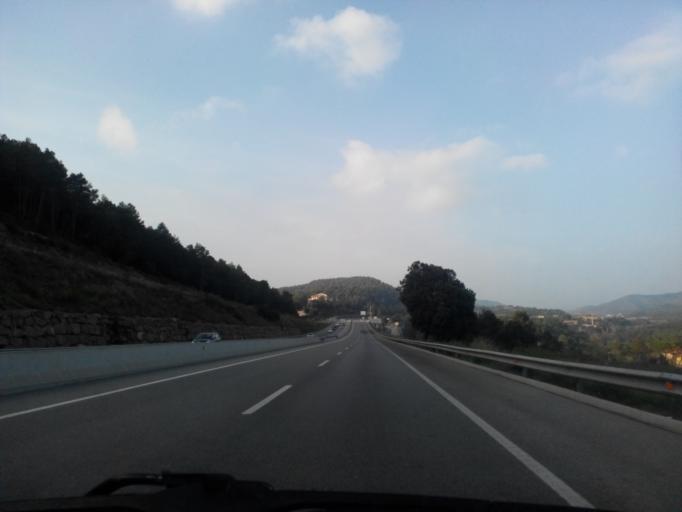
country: ES
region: Catalonia
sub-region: Provincia de Barcelona
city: Navas
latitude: 41.9281
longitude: 1.8813
